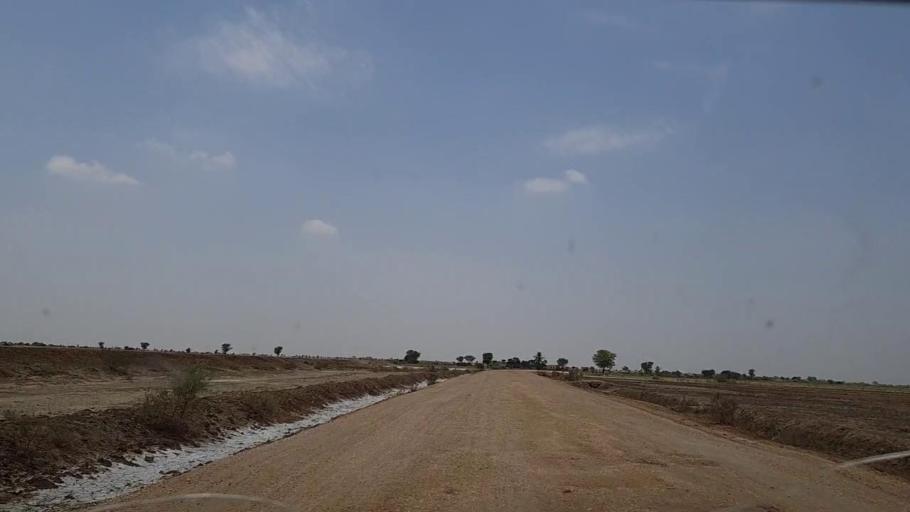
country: PK
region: Sindh
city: Phulji
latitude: 26.8019
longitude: 67.6349
